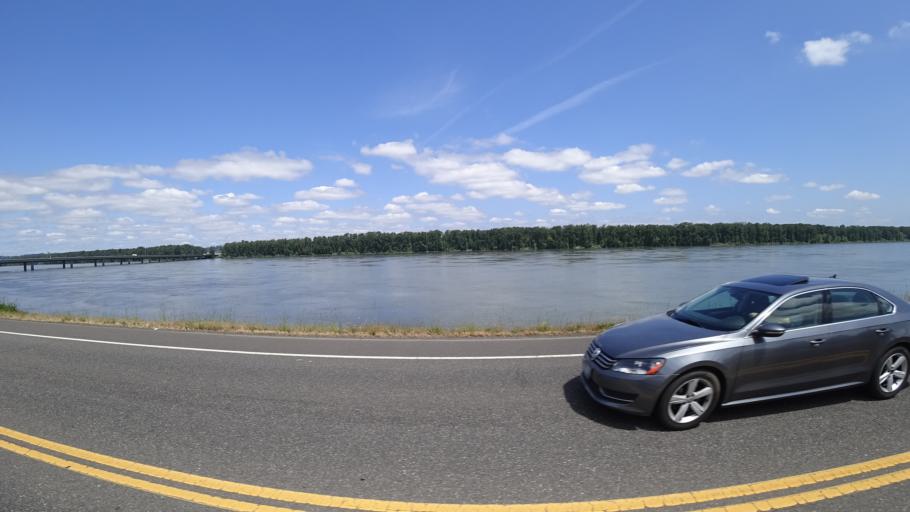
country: US
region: Washington
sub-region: Clark County
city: Mill Plain
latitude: 45.5710
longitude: -122.5409
